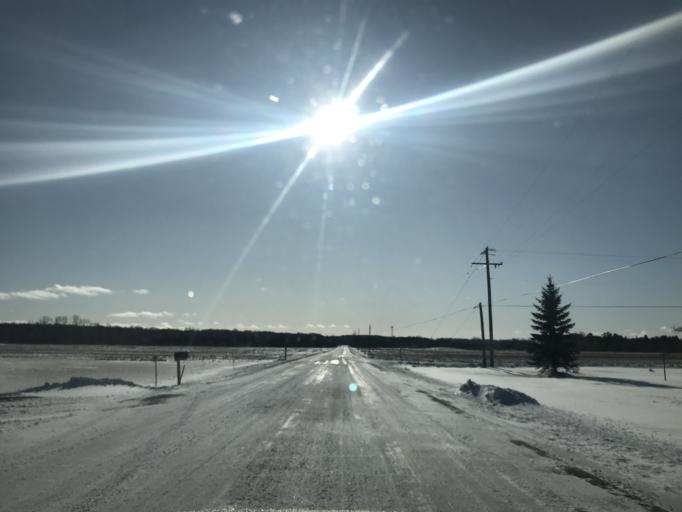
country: US
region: Wisconsin
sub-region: Door County
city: Sturgeon Bay
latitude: 44.8355
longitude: -87.5045
